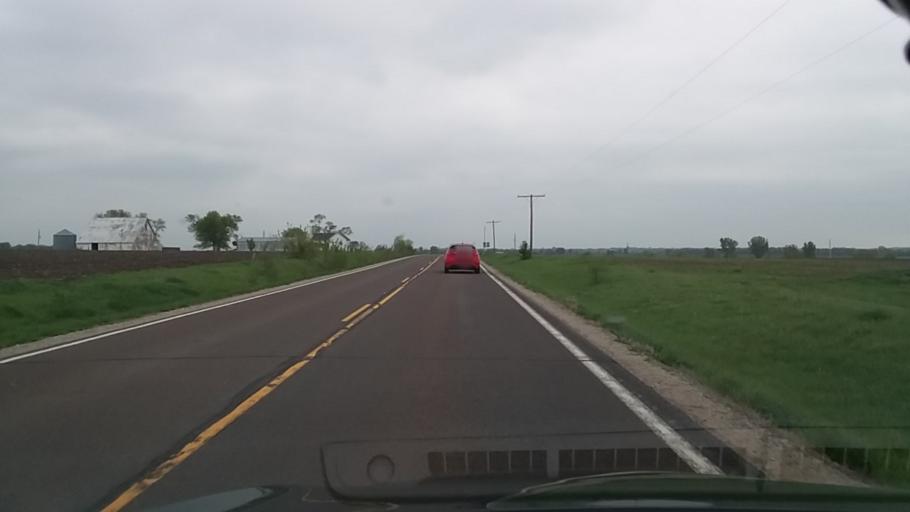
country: US
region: Kansas
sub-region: Douglas County
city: Eudora
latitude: 38.8723
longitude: -95.0933
